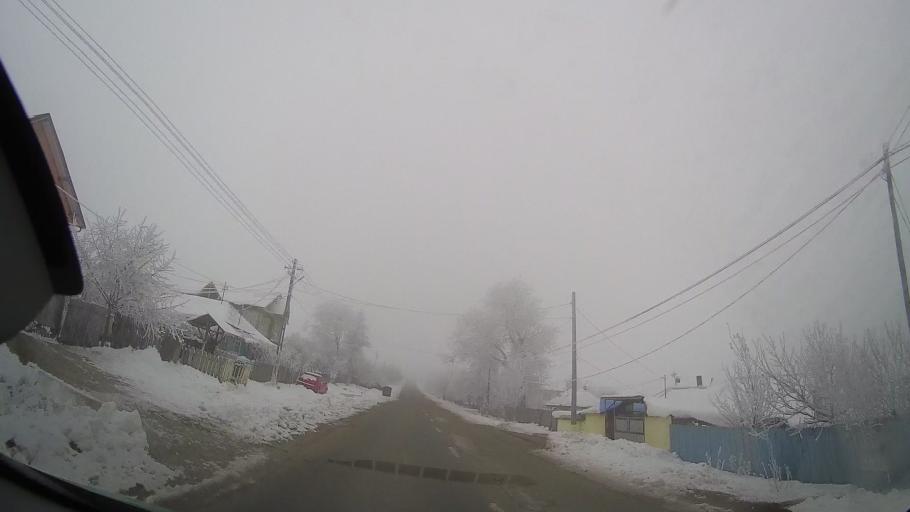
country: RO
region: Neamt
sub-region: Comuna Valea Ursului
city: Valea Ursului
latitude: 46.7989
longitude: 27.0770
